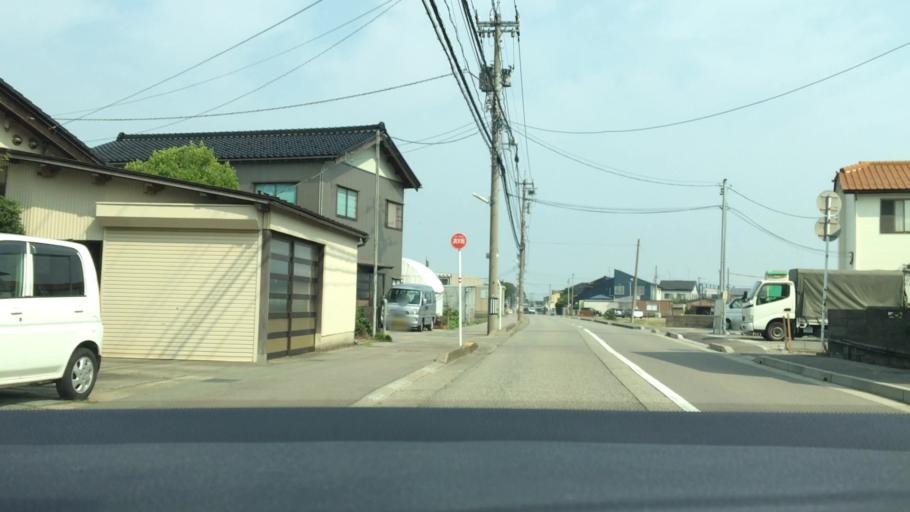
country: JP
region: Ishikawa
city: Nonoichi
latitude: 36.5160
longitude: 136.6046
